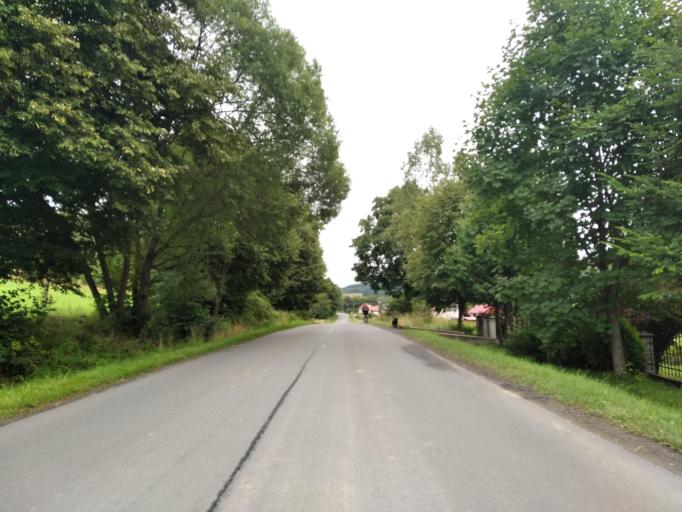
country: PL
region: Subcarpathian Voivodeship
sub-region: Powiat przemyski
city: Bircza
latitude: 49.6914
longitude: 22.4348
